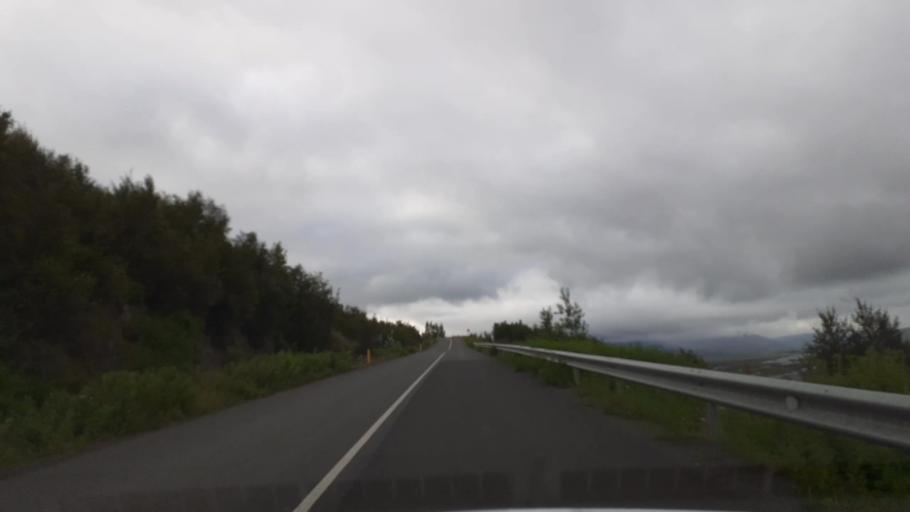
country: IS
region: Northeast
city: Akureyri
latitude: 65.6823
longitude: -18.0425
